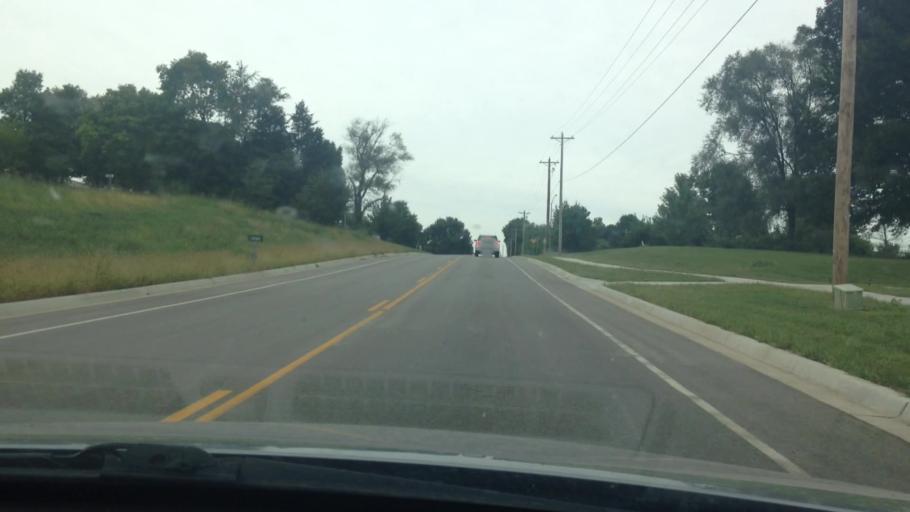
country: US
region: Missouri
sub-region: Platte County
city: Platte City
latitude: 39.3456
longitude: -94.7793
